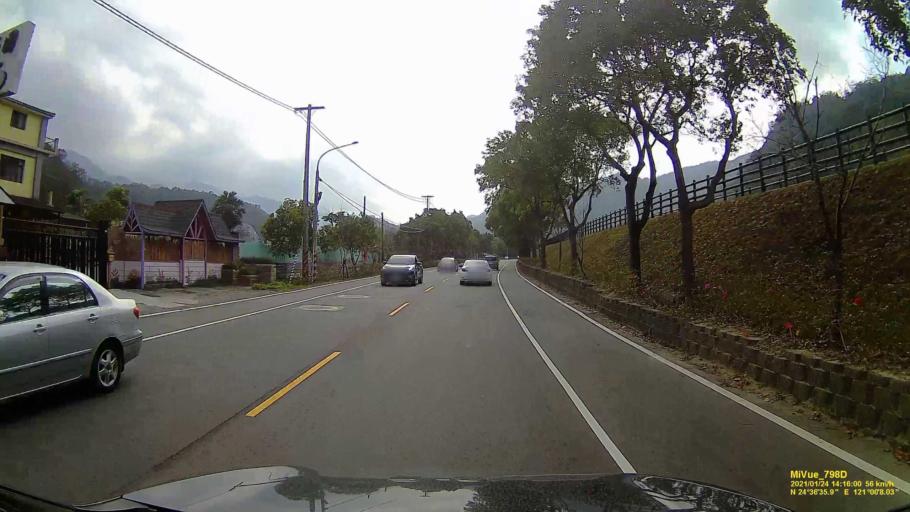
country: TW
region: Taiwan
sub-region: Miaoli
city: Miaoli
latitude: 24.6096
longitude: 121.0020
